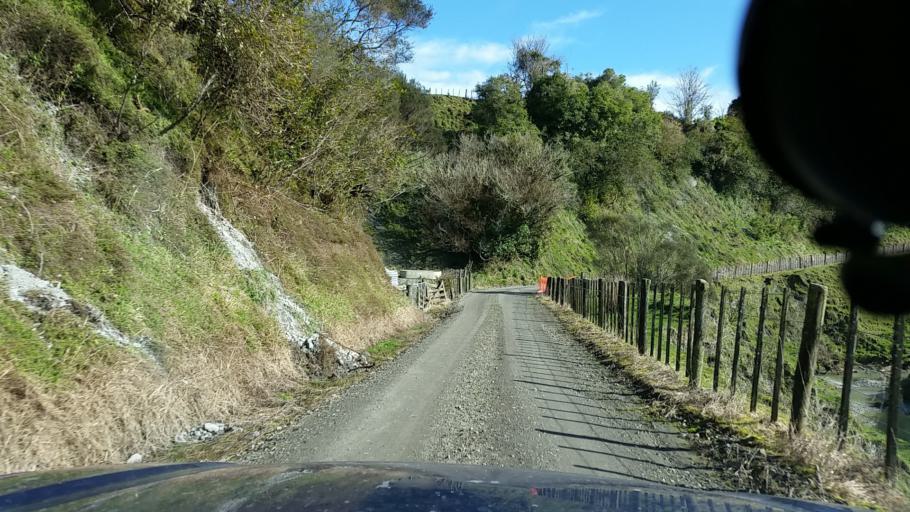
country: NZ
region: Taranaki
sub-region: New Plymouth District
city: Waitara
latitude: -39.0531
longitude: 174.7535
